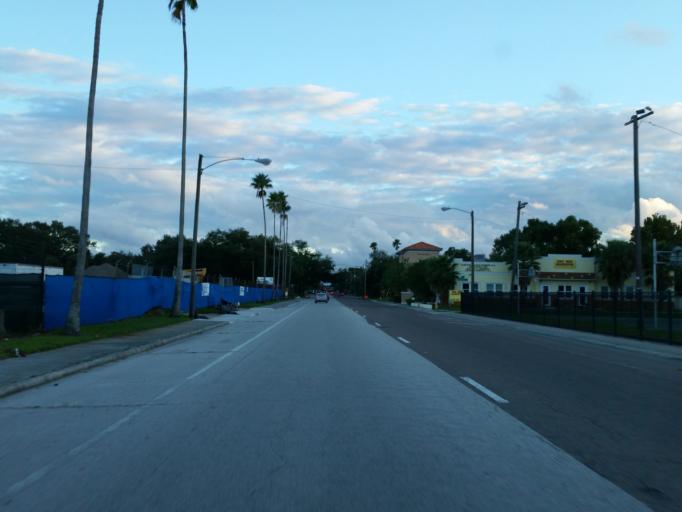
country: US
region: Florida
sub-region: Hillsborough County
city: Tampa
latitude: 27.9499
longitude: -82.4850
